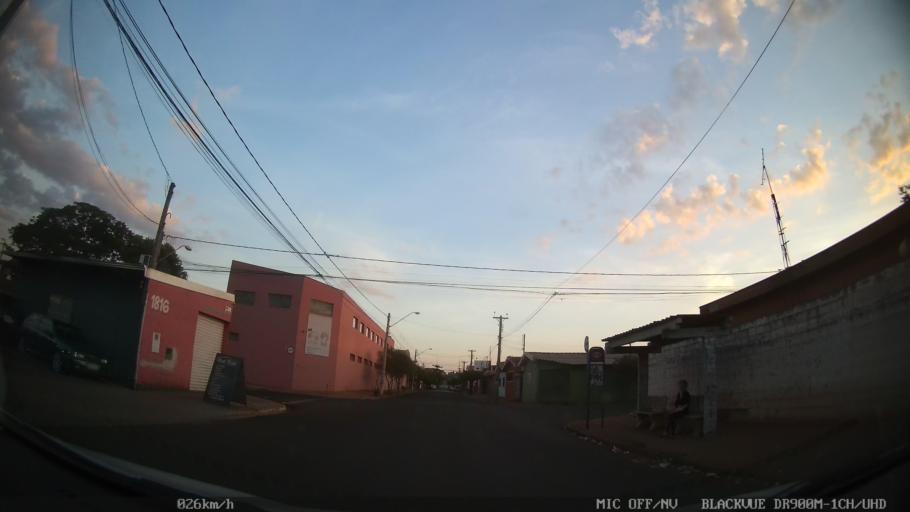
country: BR
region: Sao Paulo
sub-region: Ribeirao Preto
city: Ribeirao Preto
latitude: -21.1445
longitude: -47.8211
